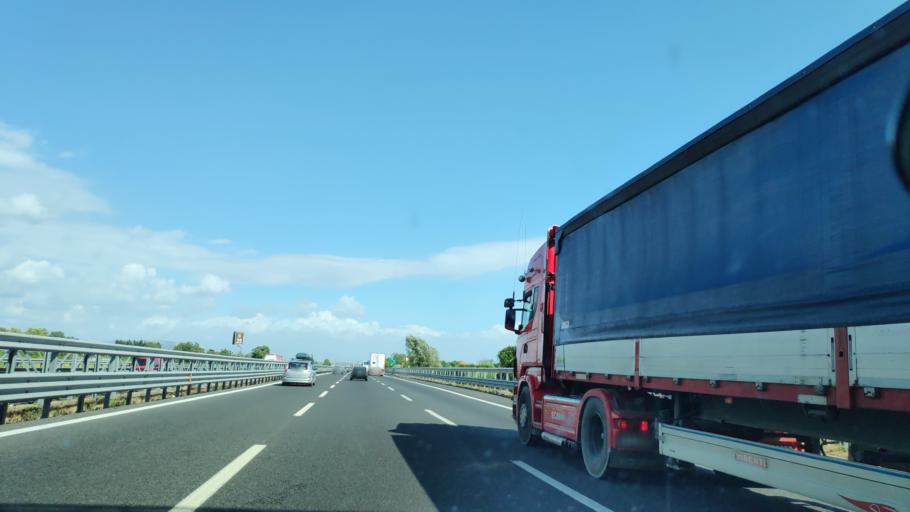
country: IT
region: Campania
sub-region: Provincia di Salerno
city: Pontecagnano
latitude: 40.6459
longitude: 14.8885
